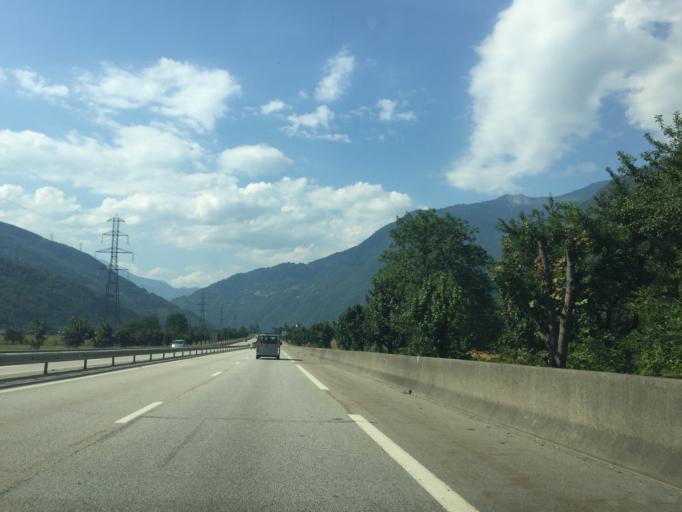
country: FR
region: Rhone-Alpes
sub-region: Departement de la Savoie
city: La Bathie
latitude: 45.6200
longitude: 6.4479
